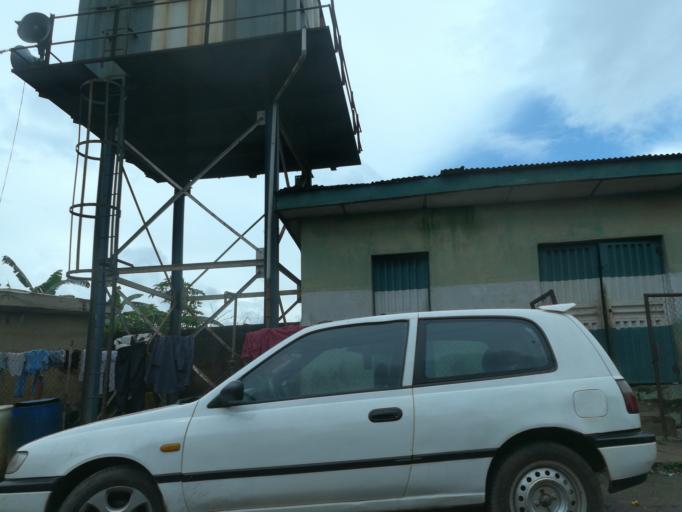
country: NG
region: Lagos
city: Agege
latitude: 6.6131
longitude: 3.3217
